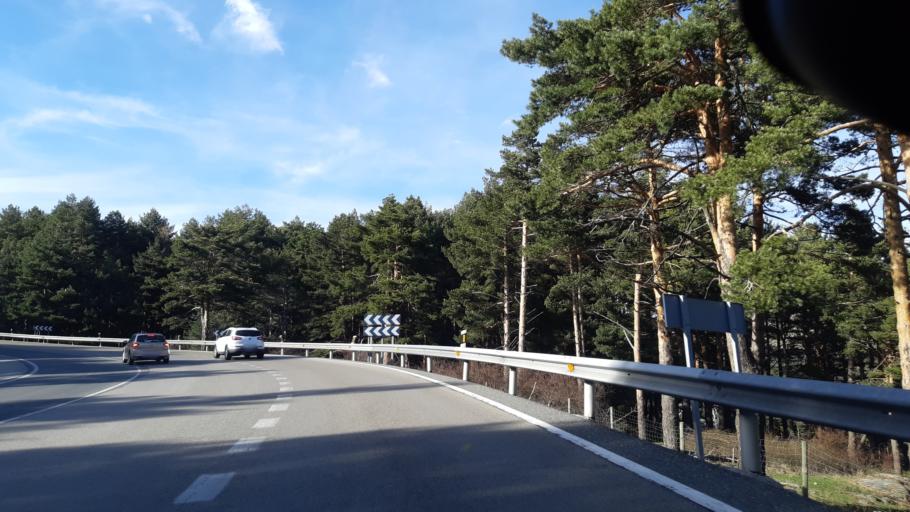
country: ES
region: Madrid
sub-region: Provincia de Madrid
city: Los Molinos
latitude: 40.7130
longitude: -4.1320
